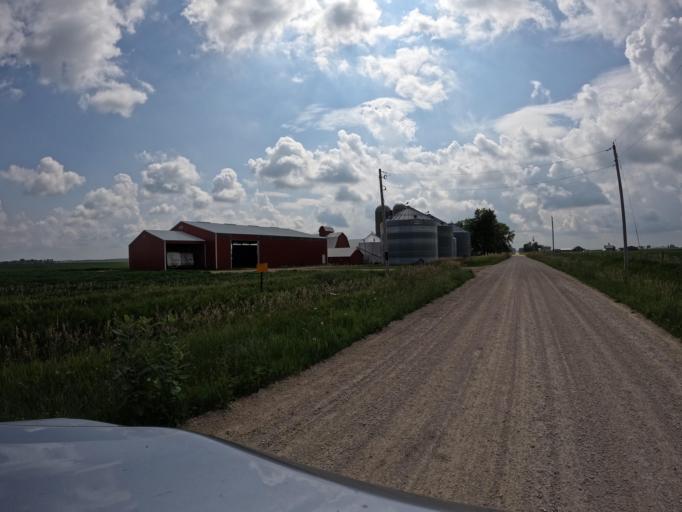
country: US
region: Iowa
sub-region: Clinton County
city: Camanche
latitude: 41.7720
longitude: -90.3371
